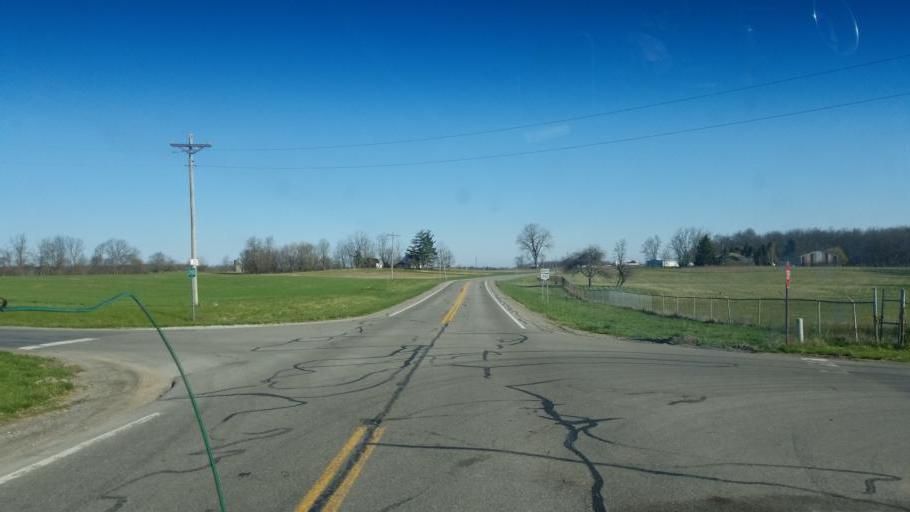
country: US
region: Ohio
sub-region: Hardin County
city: Kenton
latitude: 40.5593
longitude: -83.5872
